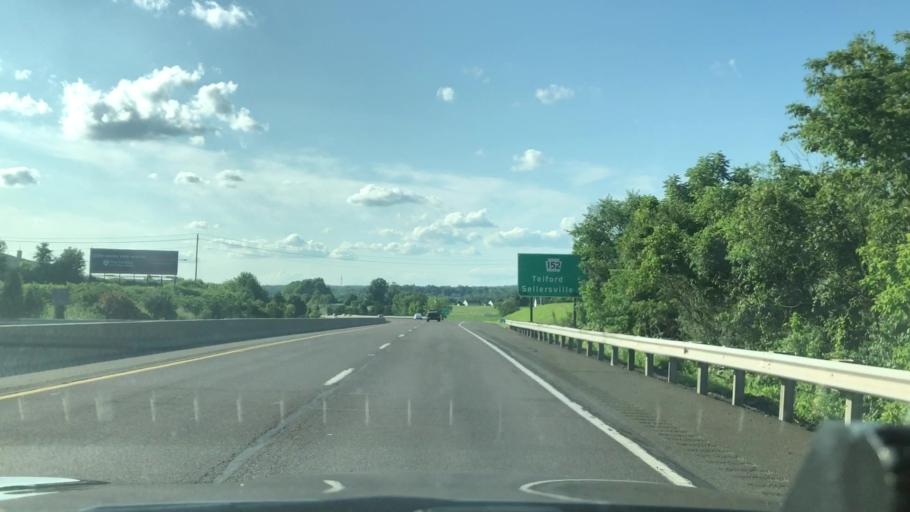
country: US
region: Pennsylvania
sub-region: Bucks County
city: Sellersville
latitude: 40.3397
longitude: -75.3147
